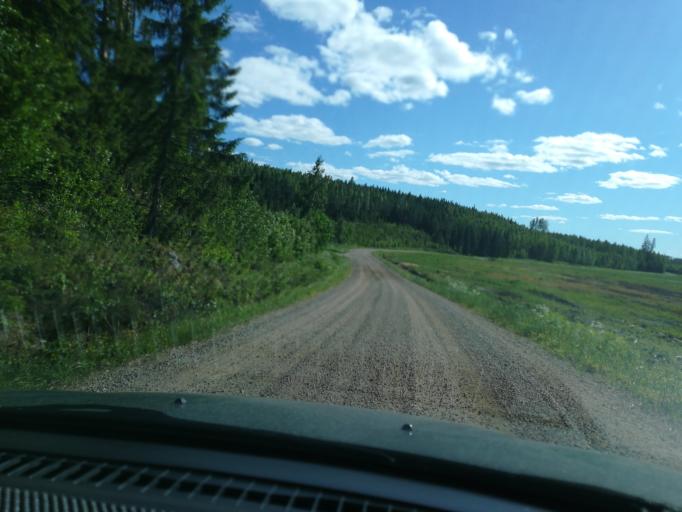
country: FI
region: Southern Savonia
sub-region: Mikkeli
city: Puumala
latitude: 61.6514
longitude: 28.1066
